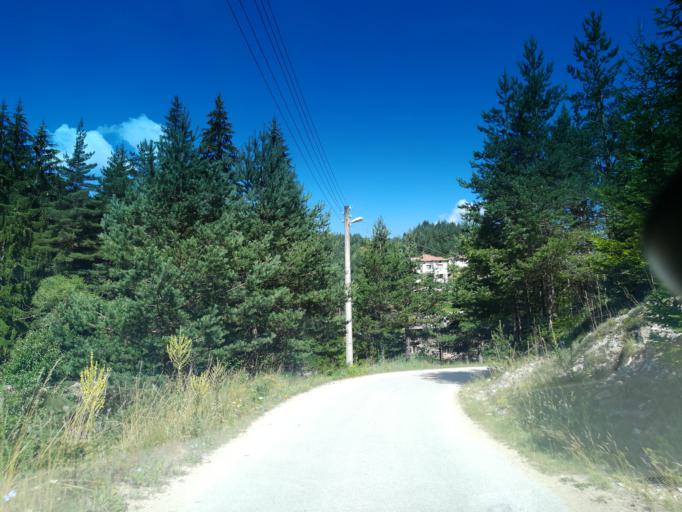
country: BG
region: Smolyan
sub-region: Obshtina Smolyan
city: Smolyan
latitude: 41.6582
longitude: 24.8192
